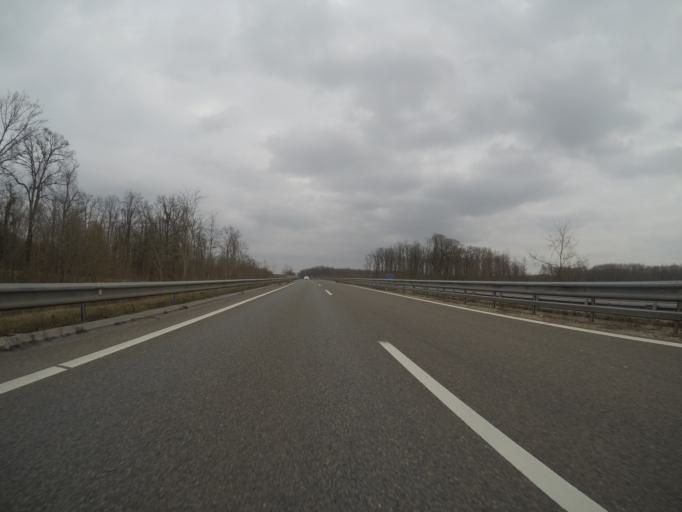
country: SI
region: Velika Polana
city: Velika Polana
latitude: 46.5968
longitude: 16.3710
